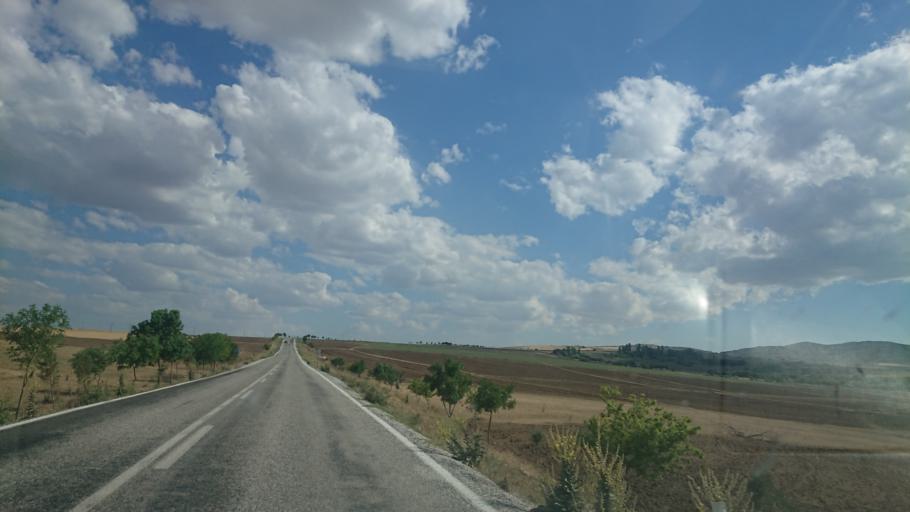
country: TR
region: Aksaray
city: Sariyahsi
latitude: 38.9547
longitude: 33.8382
